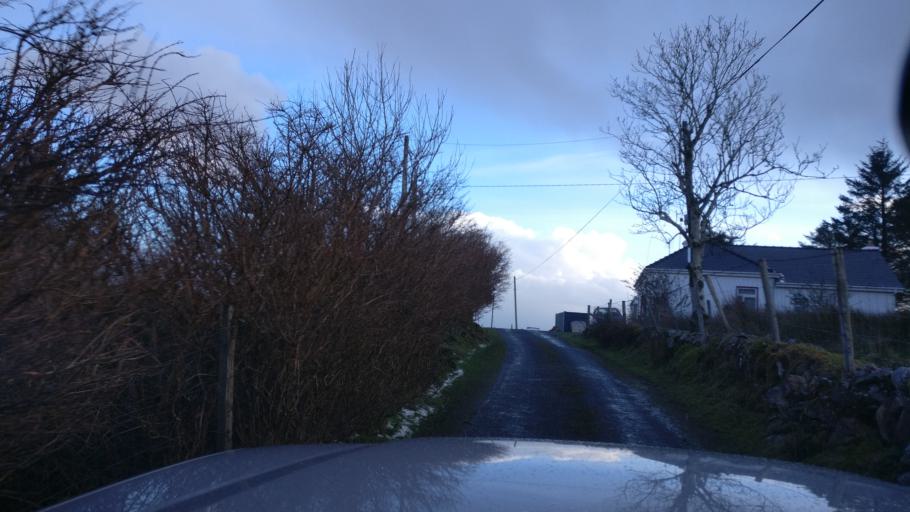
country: IE
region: Connaught
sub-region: County Galway
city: Clifden
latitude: 53.4867
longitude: -9.6979
